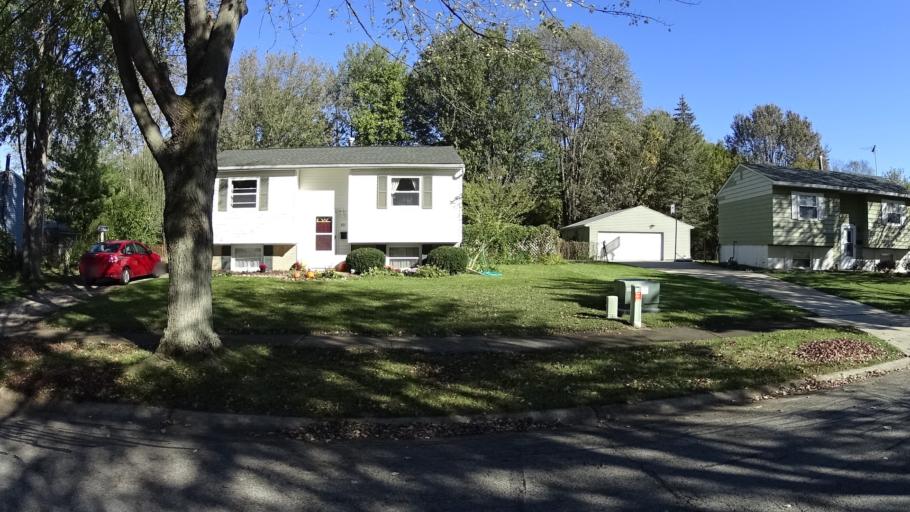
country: US
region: Ohio
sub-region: Lorain County
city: Oberlin
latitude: 41.2810
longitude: -82.2234
